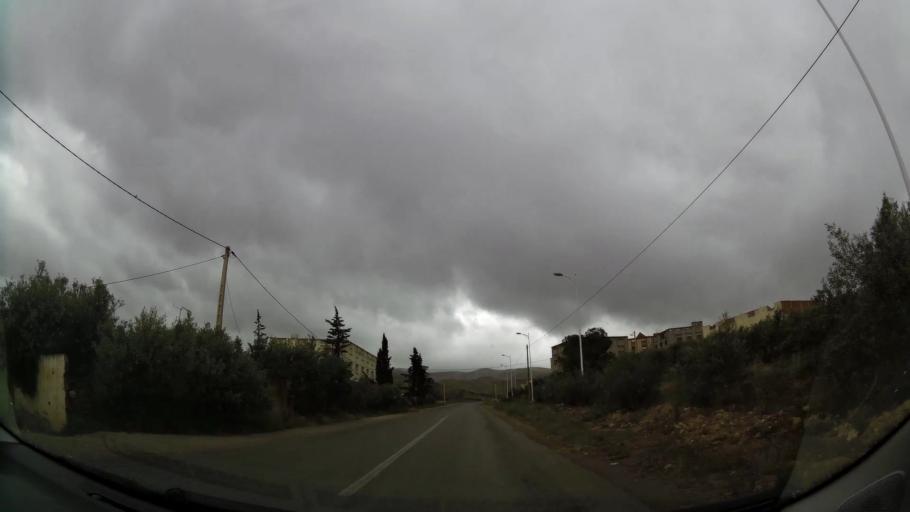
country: MA
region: Oriental
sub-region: Nador
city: Midar
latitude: 35.0580
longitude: -3.4663
